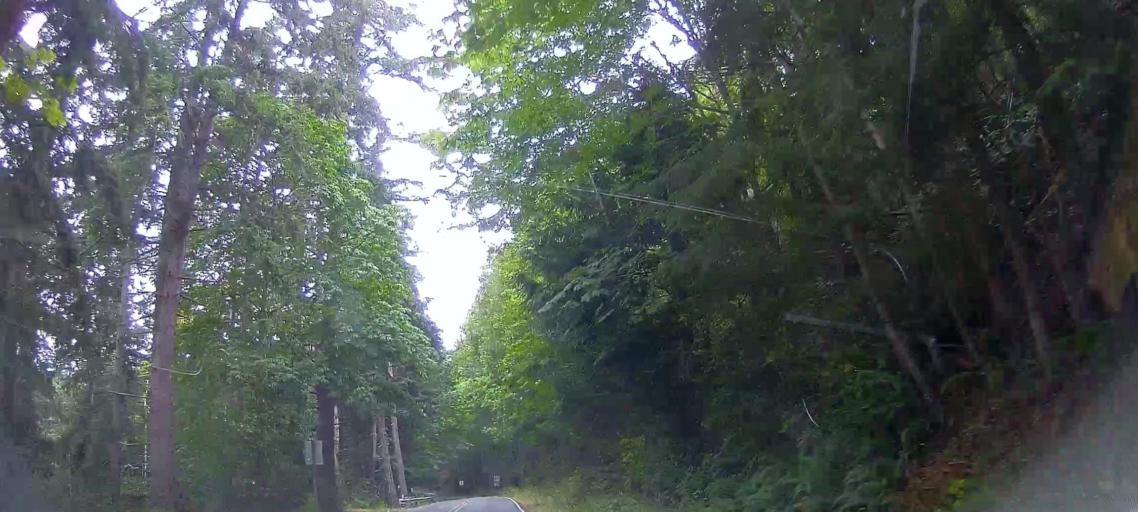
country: US
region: Washington
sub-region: Skagit County
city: Anacortes
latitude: 48.4542
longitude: -122.6340
